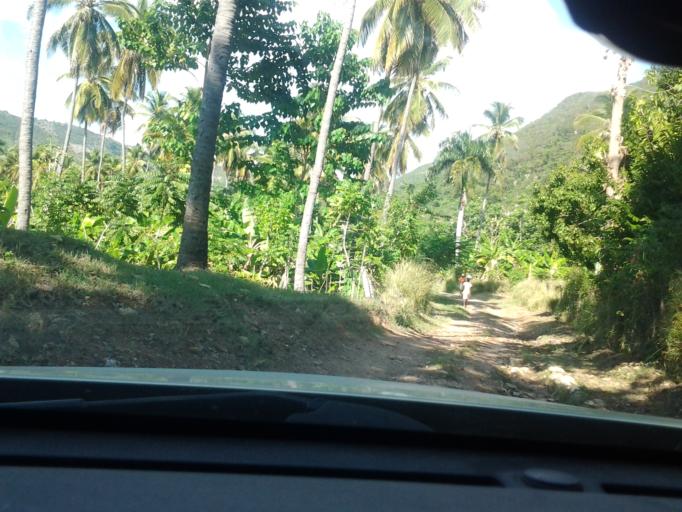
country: HT
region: Sud-Est
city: Jacmel
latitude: 18.2347
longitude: -72.4864
